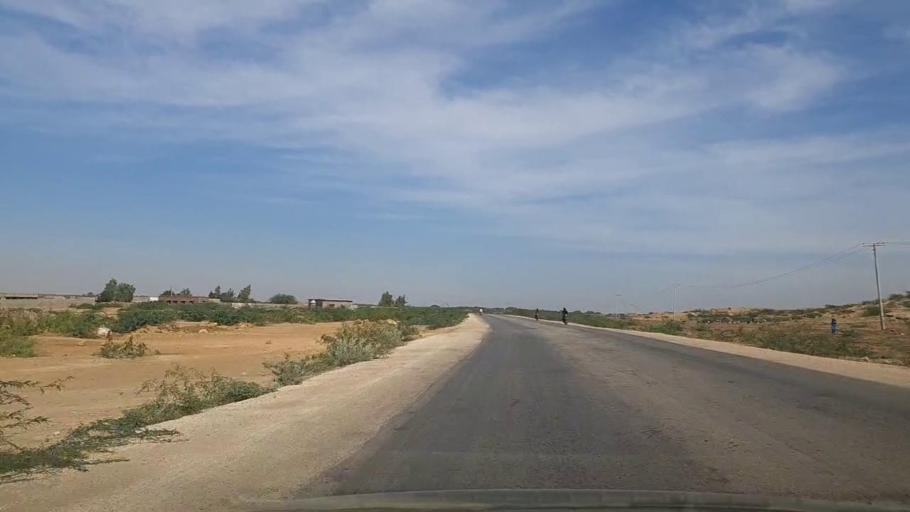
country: PK
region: Sindh
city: Daro Mehar
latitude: 24.9894
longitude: 68.1415
